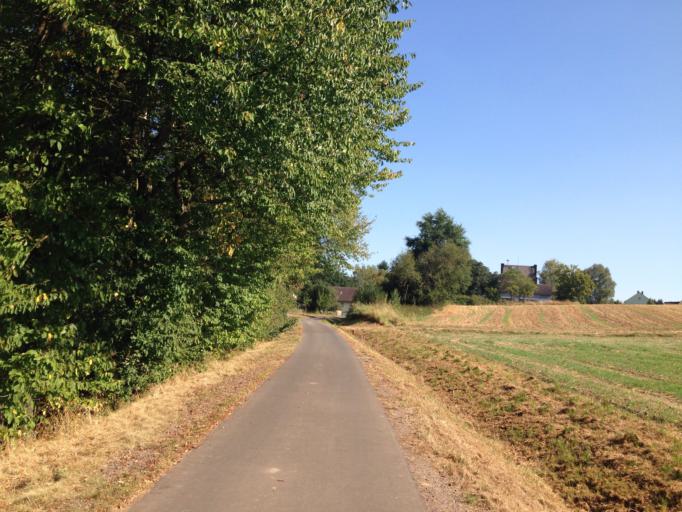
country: DE
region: Hesse
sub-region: Regierungsbezirk Giessen
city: Rabenau
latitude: 50.6619
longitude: 8.8872
